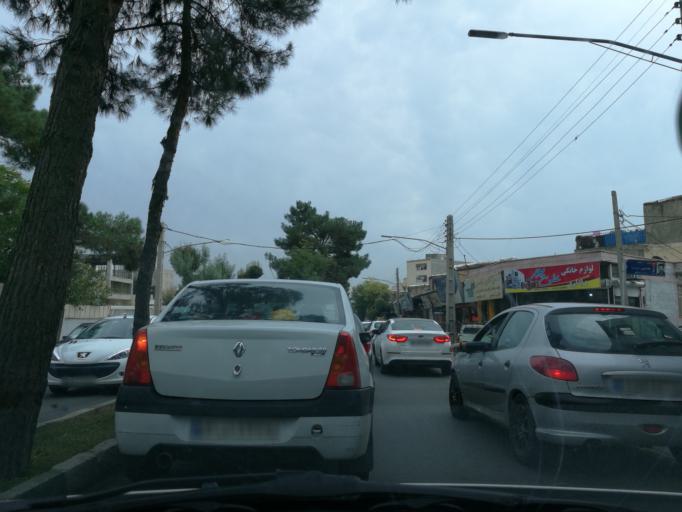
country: IR
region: Alborz
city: Karaj
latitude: 35.8487
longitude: 50.9683
